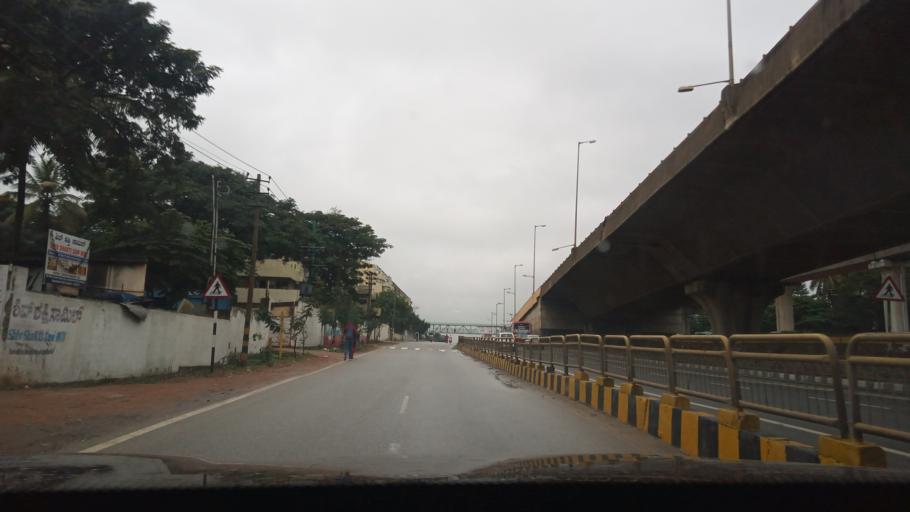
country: IN
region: Karnataka
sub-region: Bangalore Urban
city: Yelahanka
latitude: 13.0470
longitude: 77.4986
